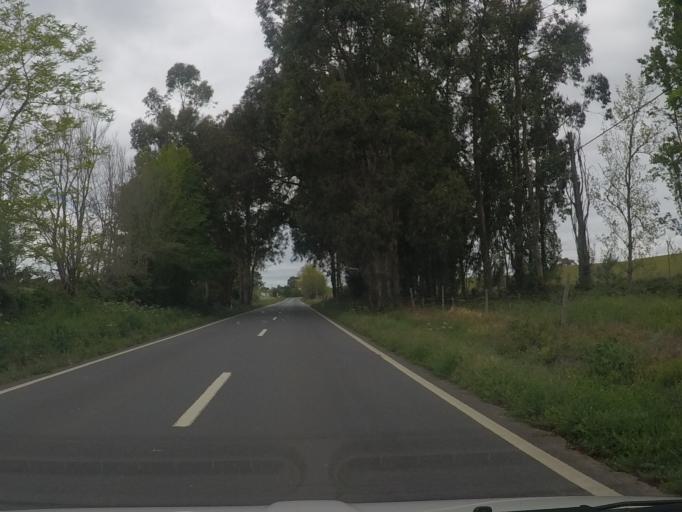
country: PT
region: Setubal
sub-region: Santiago do Cacem
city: Cercal
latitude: 37.8228
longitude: -8.6892
